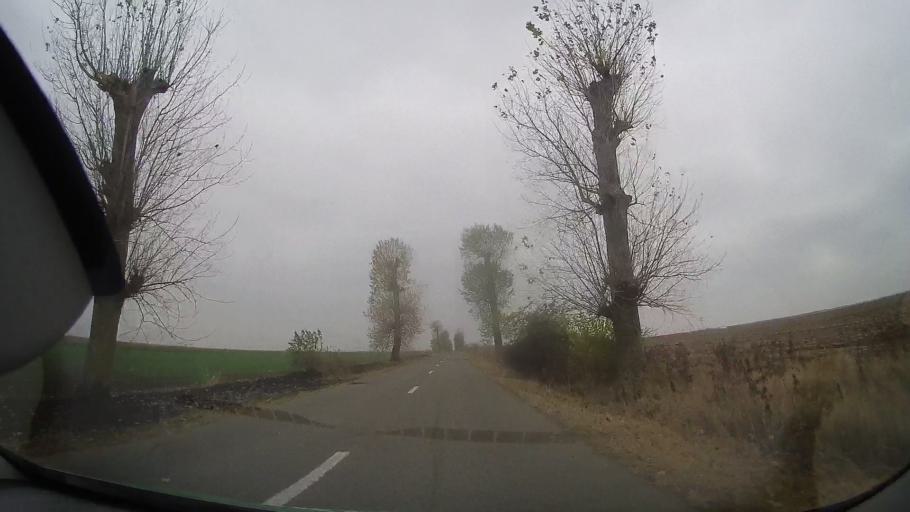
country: RO
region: Ialomita
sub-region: Comuna Grindu
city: Grindu
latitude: 44.7577
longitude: 26.8757
